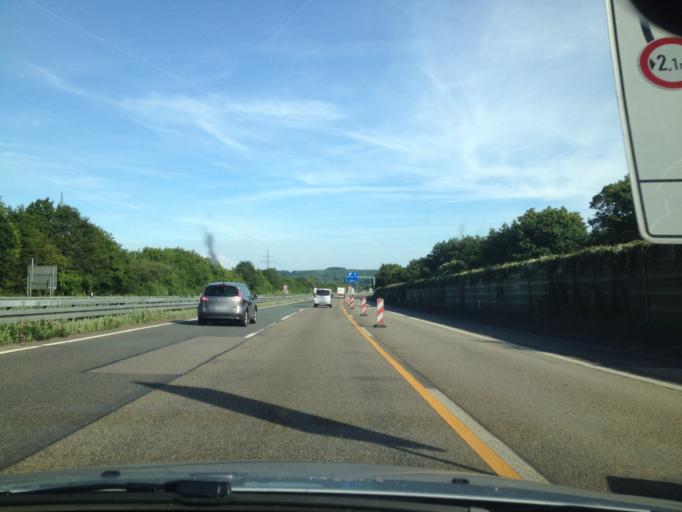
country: DE
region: Hesse
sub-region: Regierungsbezirk Giessen
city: Wetzlar
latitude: 50.5843
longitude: 8.5346
